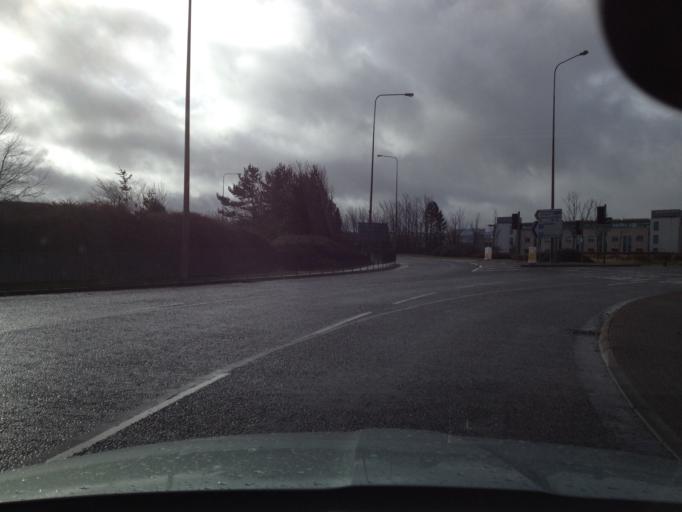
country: GB
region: Scotland
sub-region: West Lothian
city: Livingston
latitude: 55.8825
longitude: -3.5235
